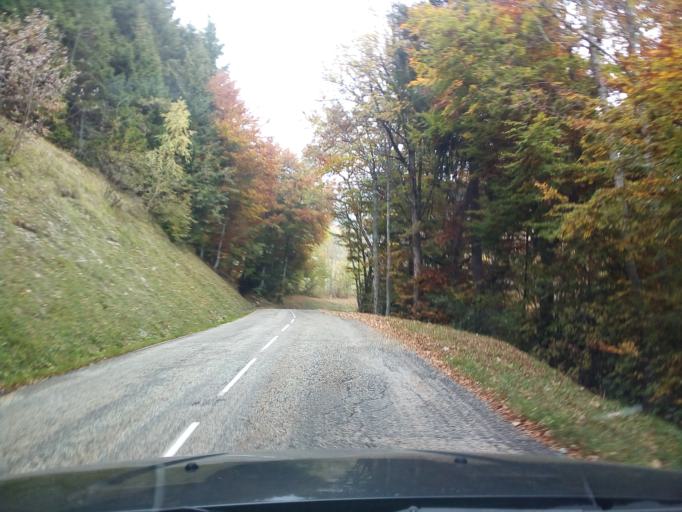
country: FR
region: Rhone-Alpes
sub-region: Departement de l'Isere
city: Bernin
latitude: 45.2955
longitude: 5.8412
